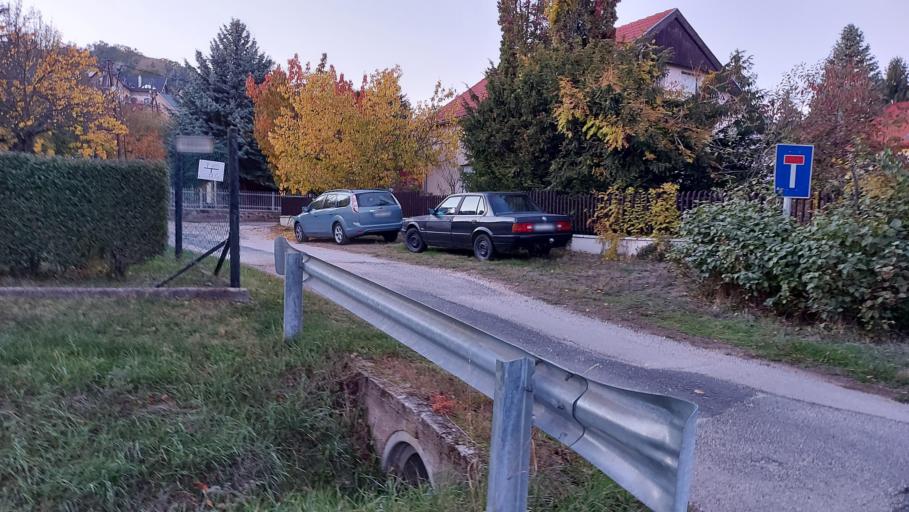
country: HU
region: Veszprem
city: Balatonalmadi
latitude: 47.0206
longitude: 18.0025
